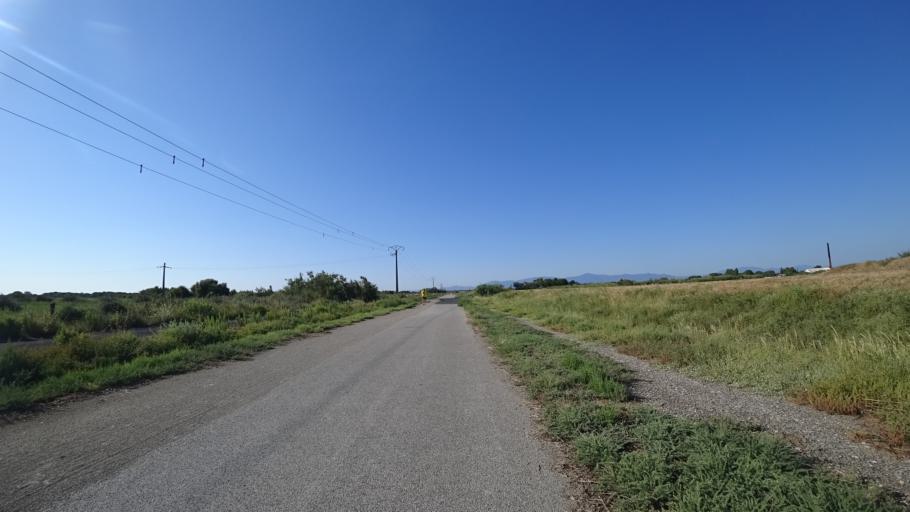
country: FR
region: Languedoc-Roussillon
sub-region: Departement des Pyrenees-Orientales
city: Sainte-Marie-Plage
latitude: 42.7490
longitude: 3.0224
